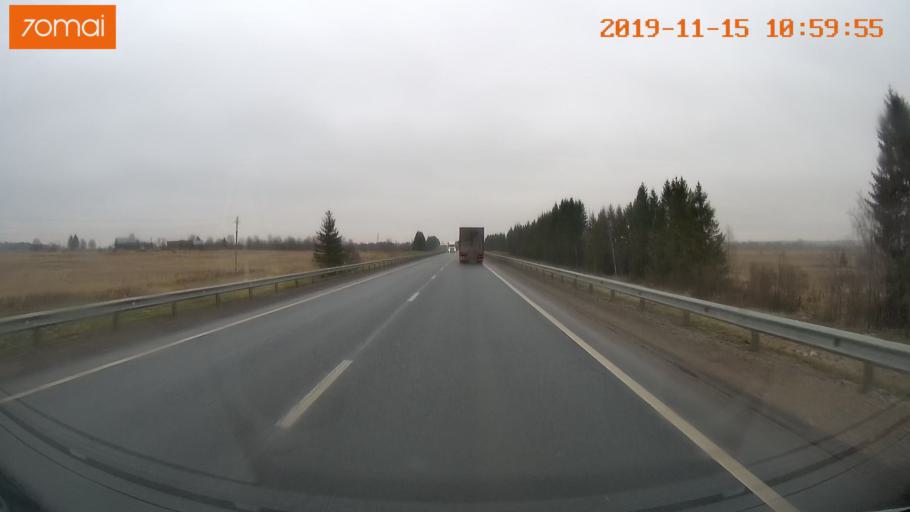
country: RU
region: Vologda
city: Chebsara
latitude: 59.1396
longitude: 38.8882
